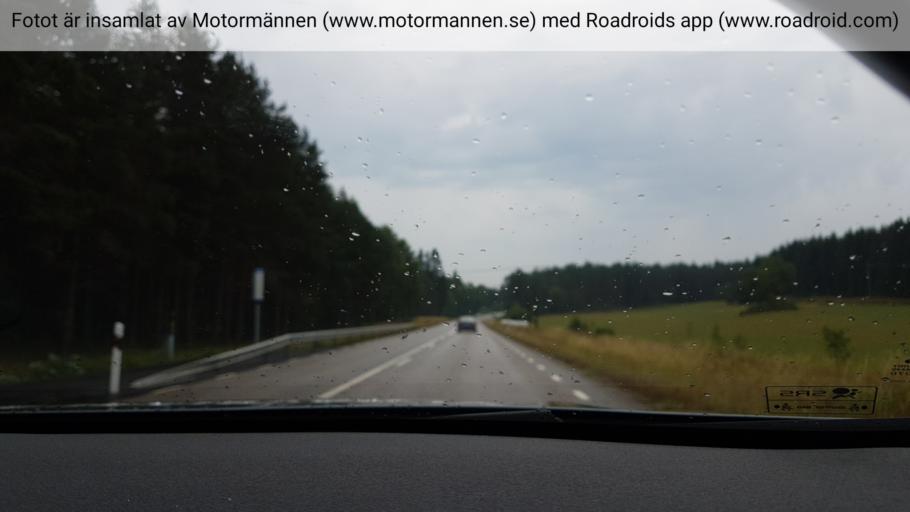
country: SE
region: Joenkoeping
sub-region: Vaggeryds Kommun
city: Vaggeryd
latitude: 57.5360
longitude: 14.2700
